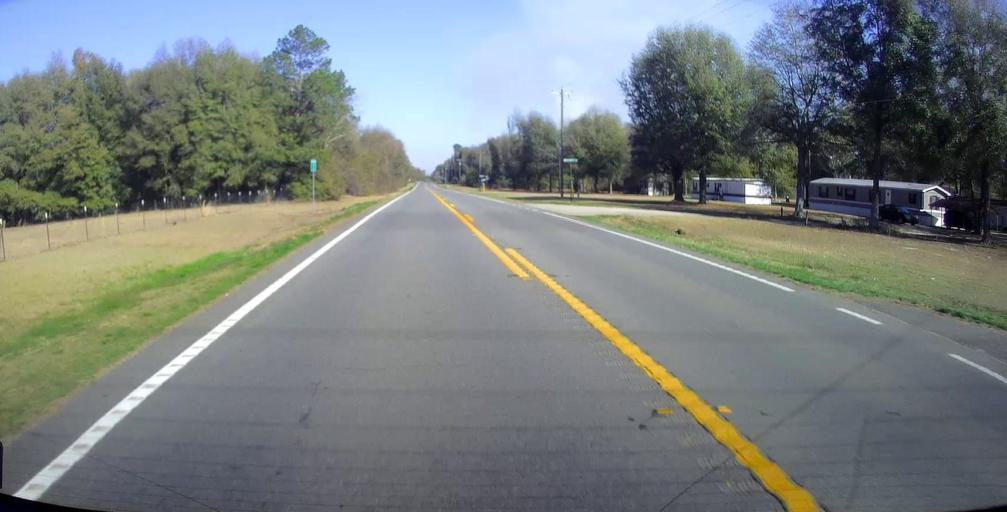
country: US
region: Georgia
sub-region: Macon County
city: Oglethorpe
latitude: 32.3298
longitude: -84.0861
